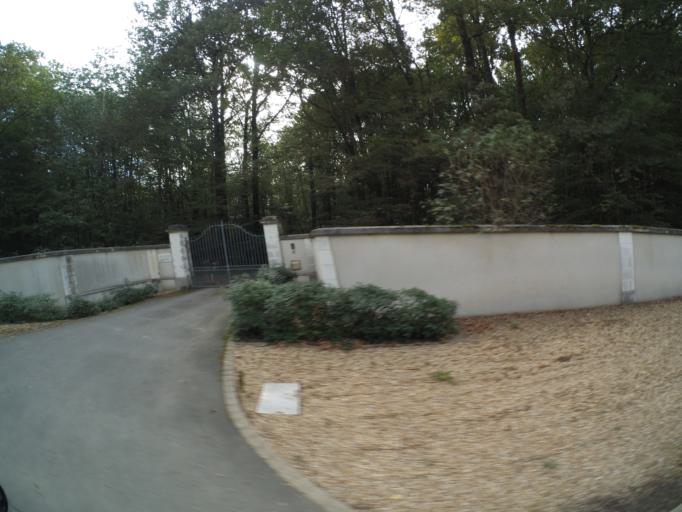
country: FR
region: Pays de la Loire
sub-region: Departement de Maine-et-Loire
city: La Chapelle-du-Genet
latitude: 47.1561
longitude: -1.0328
